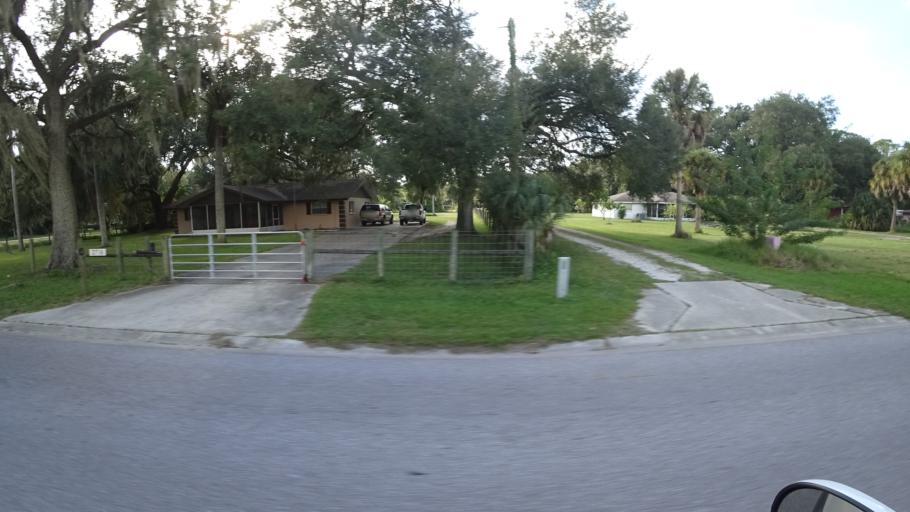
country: US
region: Florida
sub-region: Manatee County
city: Samoset
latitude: 27.4752
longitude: -82.5057
